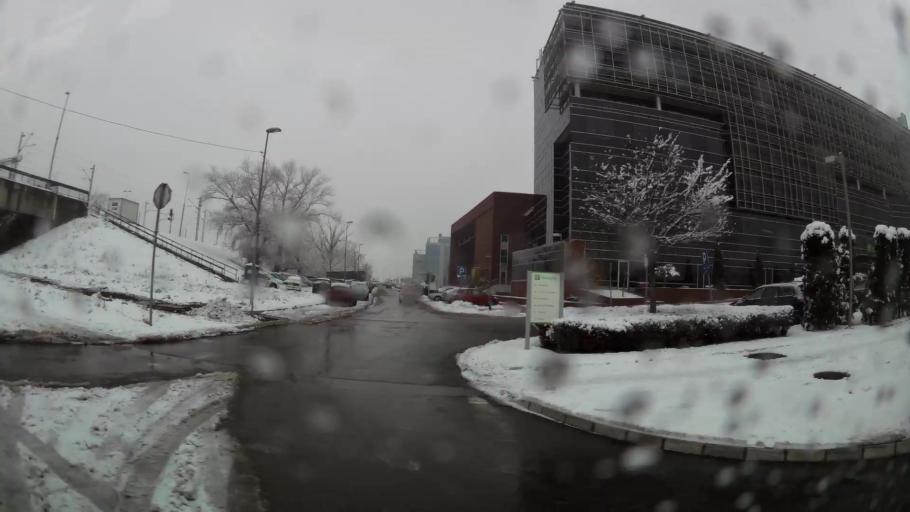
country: RS
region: Central Serbia
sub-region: Belgrade
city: Novi Beograd
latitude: 44.8092
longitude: 20.4144
